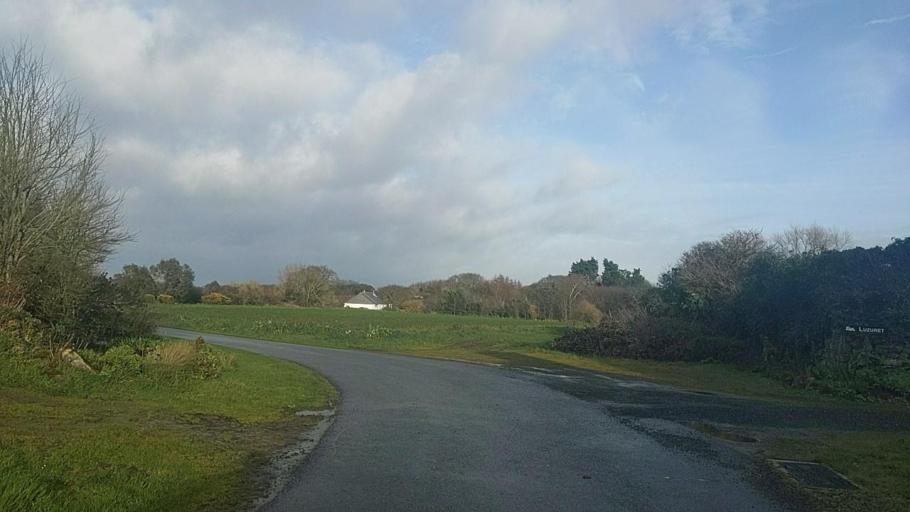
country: FR
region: Brittany
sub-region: Departement des Cotes-d'Armor
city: Pleubian
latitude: 48.8412
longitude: -3.1768
